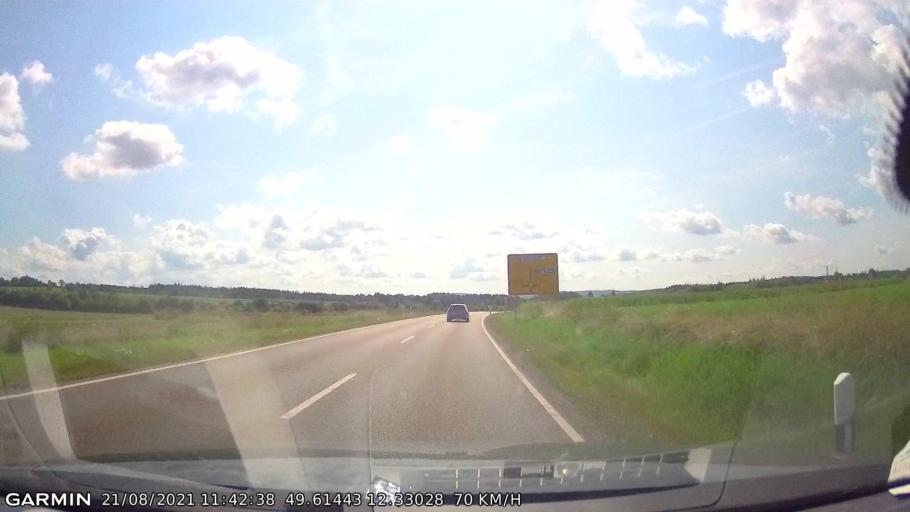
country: DE
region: Bavaria
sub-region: Upper Palatinate
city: Vohenstrauss
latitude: 49.6143
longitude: 12.3303
